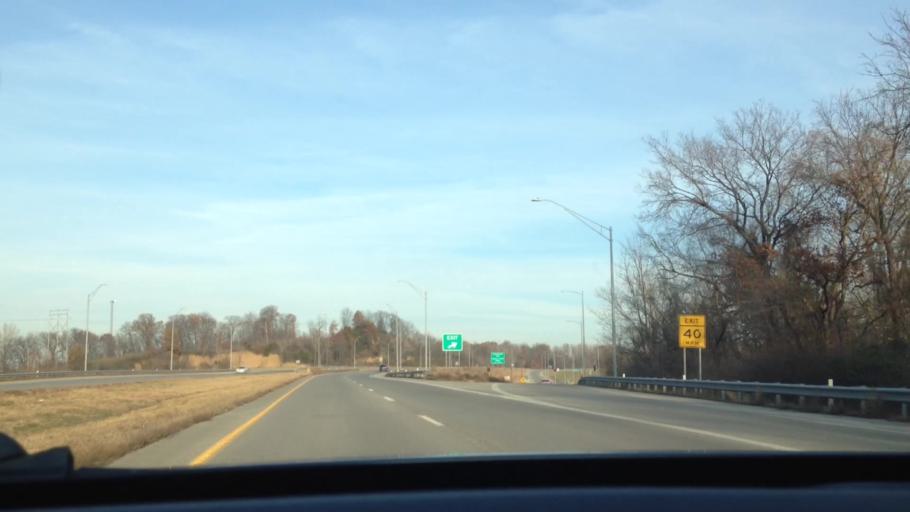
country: US
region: Missouri
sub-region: Clay County
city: North Kansas City
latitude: 39.1500
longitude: -94.5394
